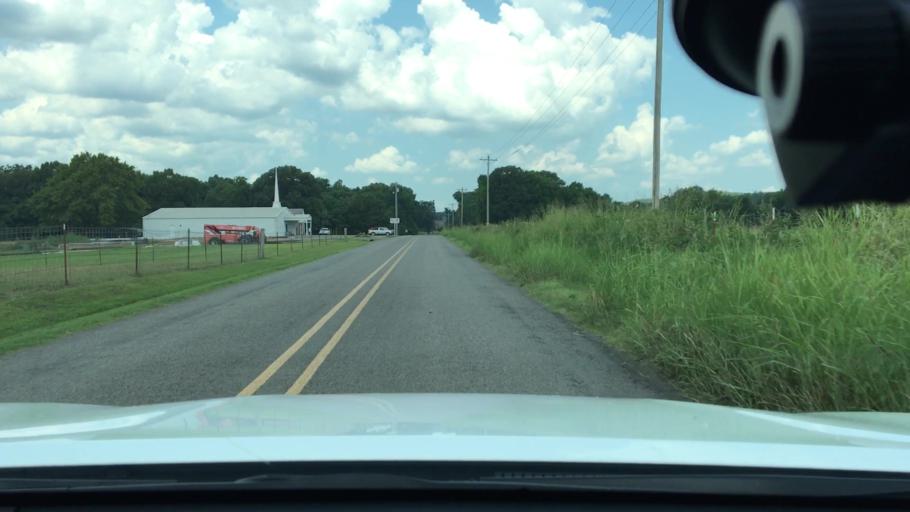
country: US
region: Arkansas
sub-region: Logan County
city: Paris
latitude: 35.2690
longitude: -93.6582
